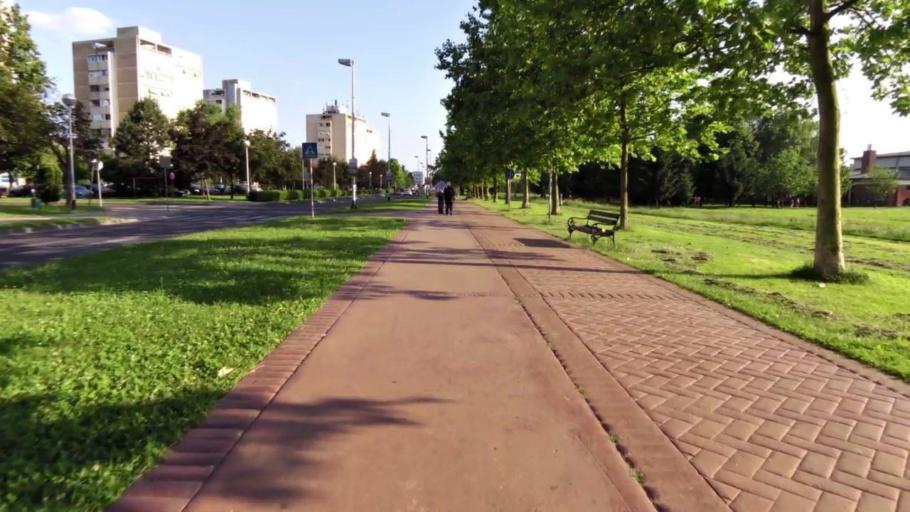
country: HR
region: Grad Zagreb
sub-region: Sesvete
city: Sesvete
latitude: 45.8310
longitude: 16.1069
